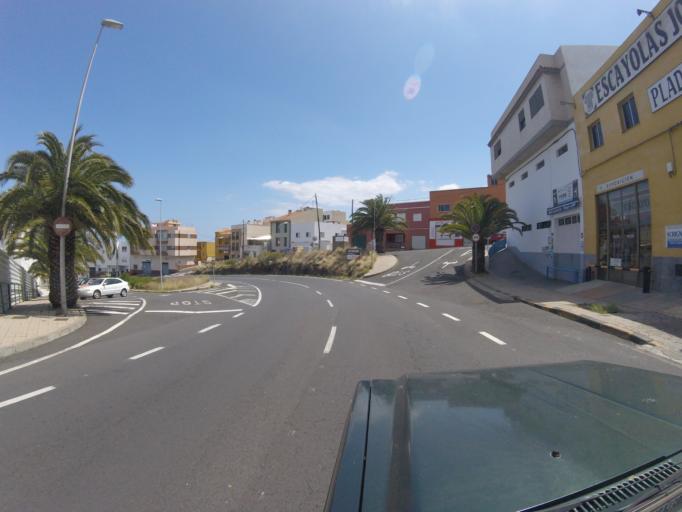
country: ES
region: Canary Islands
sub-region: Provincia de Santa Cruz de Tenerife
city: La Laguna
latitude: 28.4389
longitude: -16.3108
